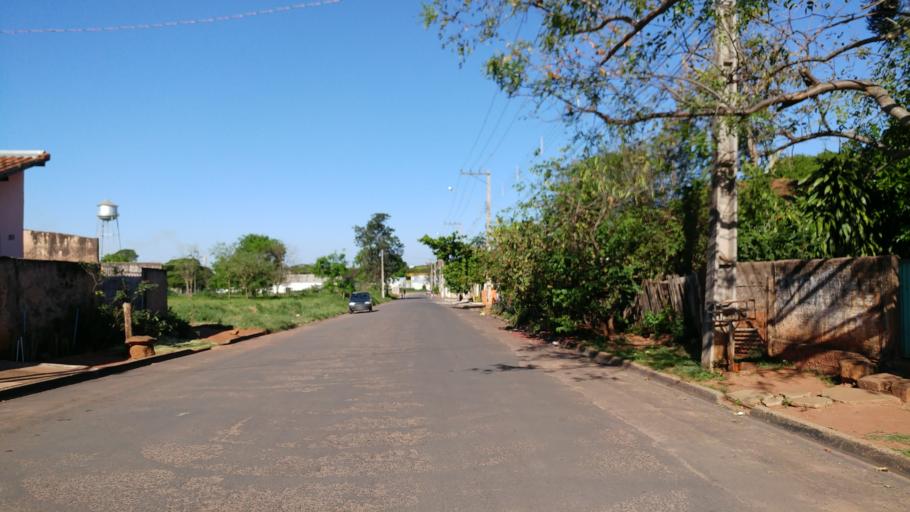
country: BR
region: Sao Paulo
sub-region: Paraguacu Paulista
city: Paraguacu Paulista
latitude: -22.4240
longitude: -50.5745
